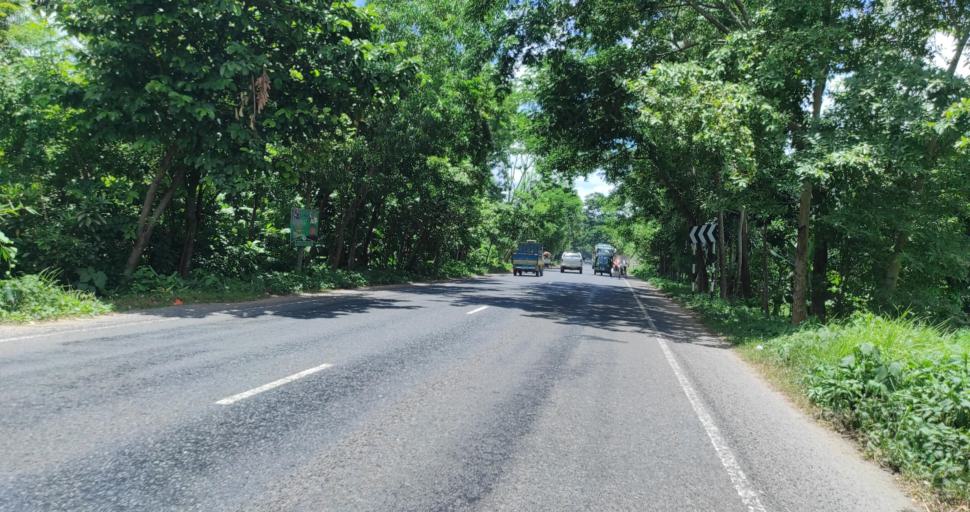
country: BD
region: Barisal
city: Gaurnadi
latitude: 22.8358
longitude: 90.2533
